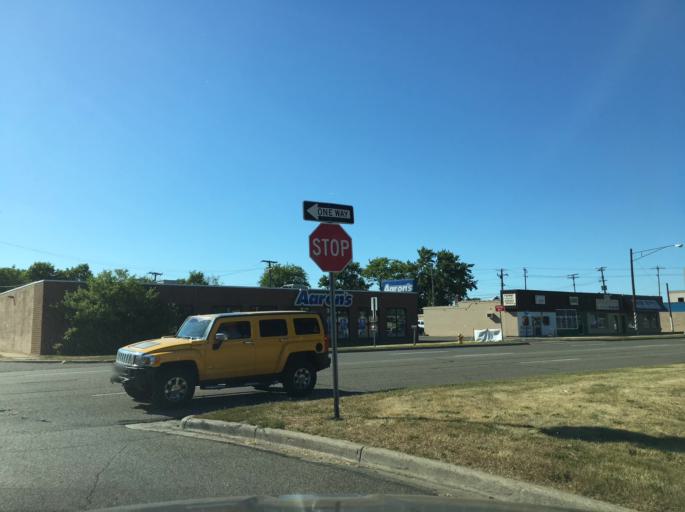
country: US
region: Michigan
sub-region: Macomb County
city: Clinton
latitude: 42.5530
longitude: -82.9005
